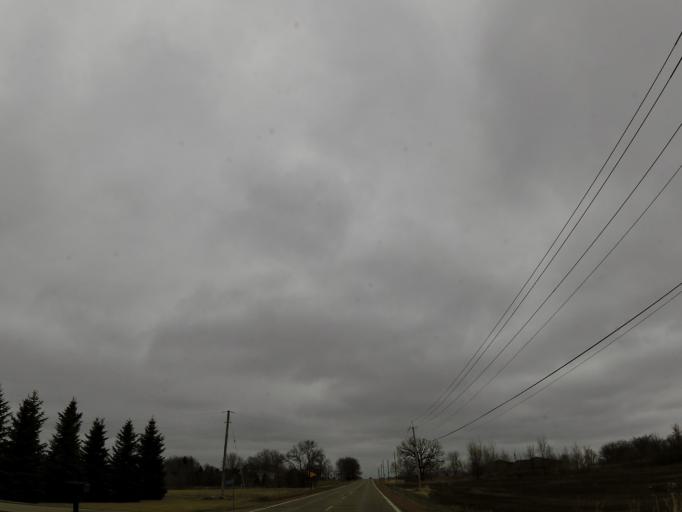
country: US
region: Minnesota
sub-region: Scott County
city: Shakopee
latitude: 44.7694
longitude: -93.5409
